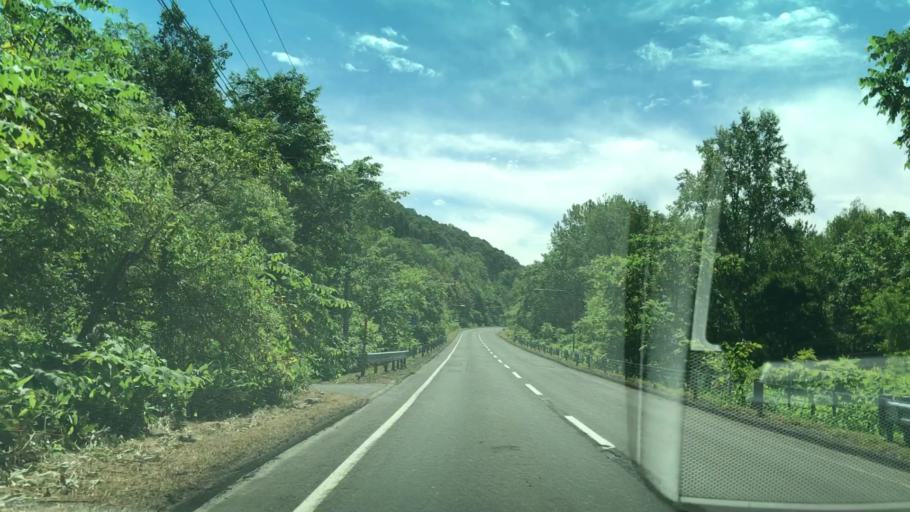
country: JP
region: Hokkaido
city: Shimo-furano
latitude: 42.9693
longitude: 142.4247
